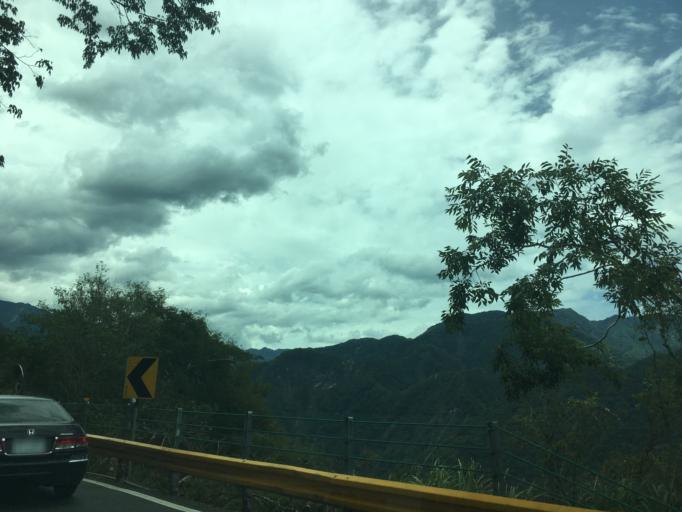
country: TW
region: Taiwan
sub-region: Hualien
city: Hualian
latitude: 24.1903
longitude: 121.4857
